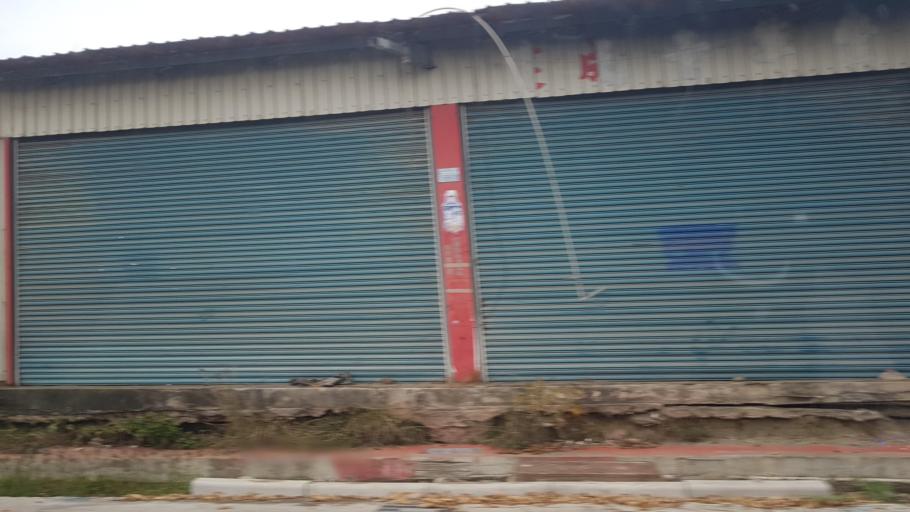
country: TW
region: Taiwan
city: Xinying
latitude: 23.3159
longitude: 120.3026
